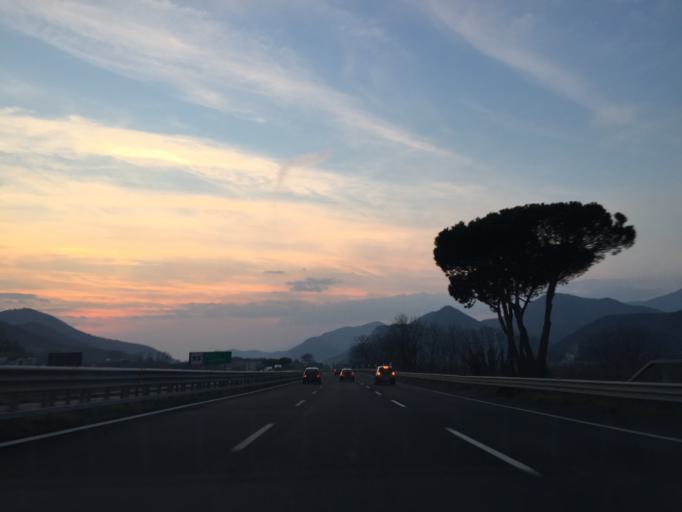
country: IT
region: Campania
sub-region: Provincia di Salerno
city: Faraldo-Nocelleto
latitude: 40.7738
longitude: 14.7656
